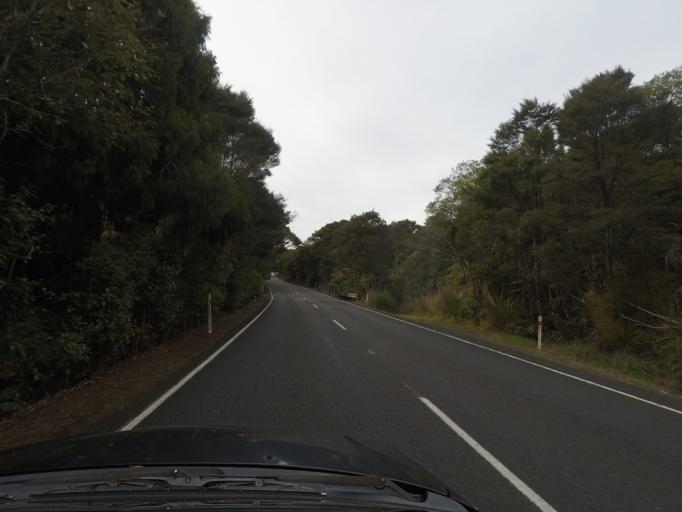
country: NZ
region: Auckland
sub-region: Auckland
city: Titirangi
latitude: -36.9337
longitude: 174.5664
